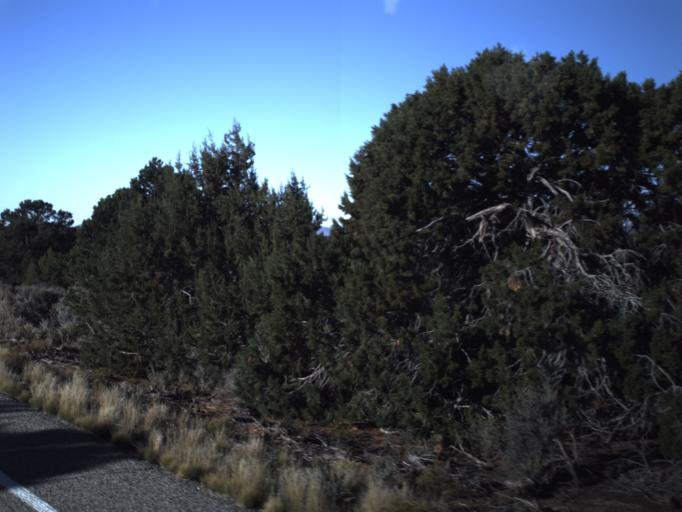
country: US
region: Utah
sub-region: San Juan County
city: Blanding
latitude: 37.5747
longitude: -109.9211
